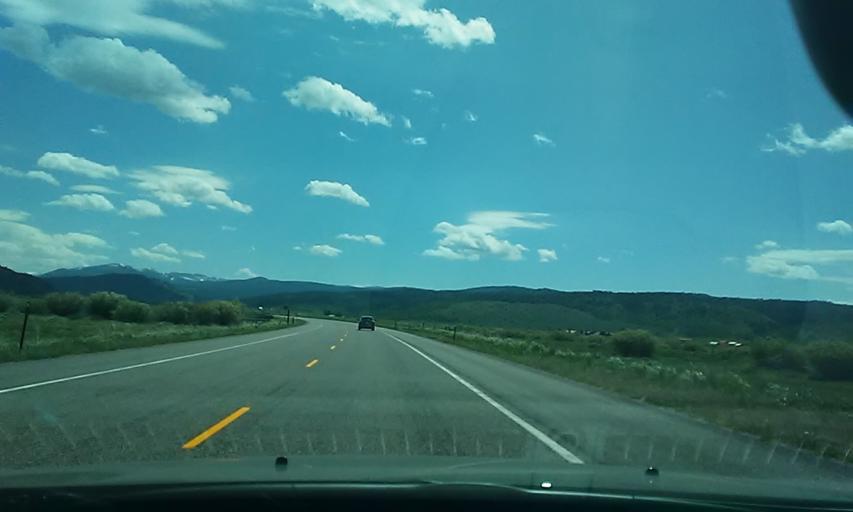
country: US
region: Wyoming
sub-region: Teton County
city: Jackson
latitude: 43.8329
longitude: -110.4241
